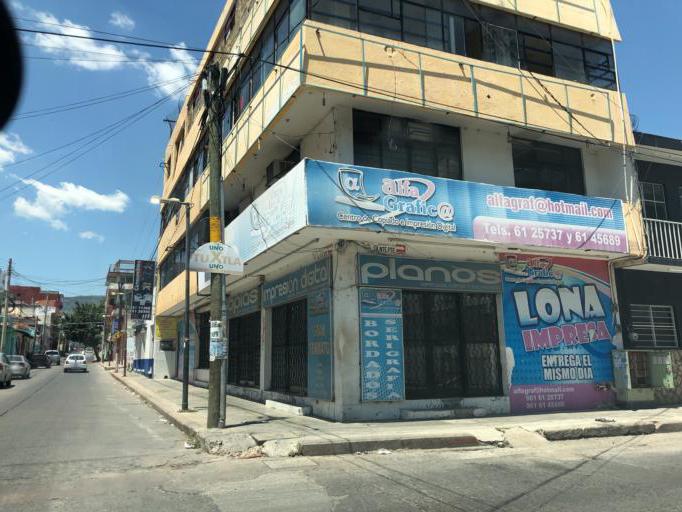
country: MX
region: Chiapas
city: Tuxtla Gutierrez
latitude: 16.7562
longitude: -93.1200
